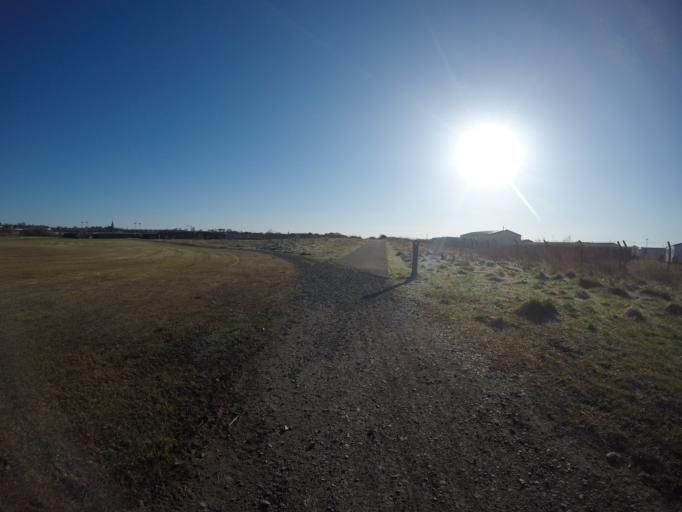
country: GB
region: Scotland
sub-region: North Ayrshire
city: Stevenston
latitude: 55.6344
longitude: -4.7639
